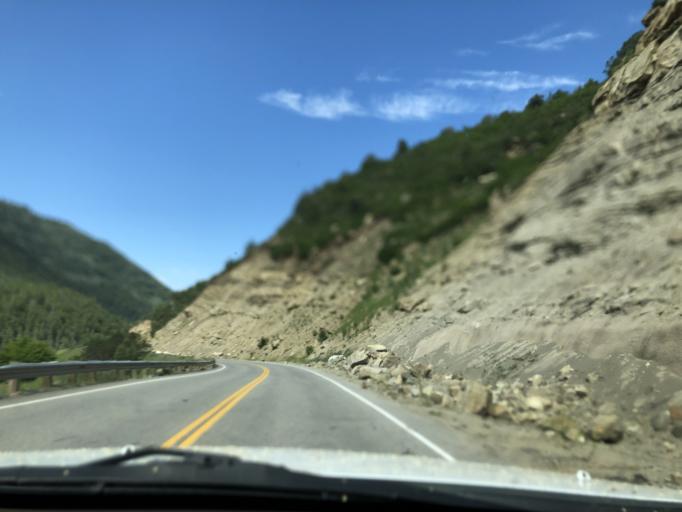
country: US
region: Colorado
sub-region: Delta County
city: Paonia
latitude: 38.9428
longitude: -107.3542
